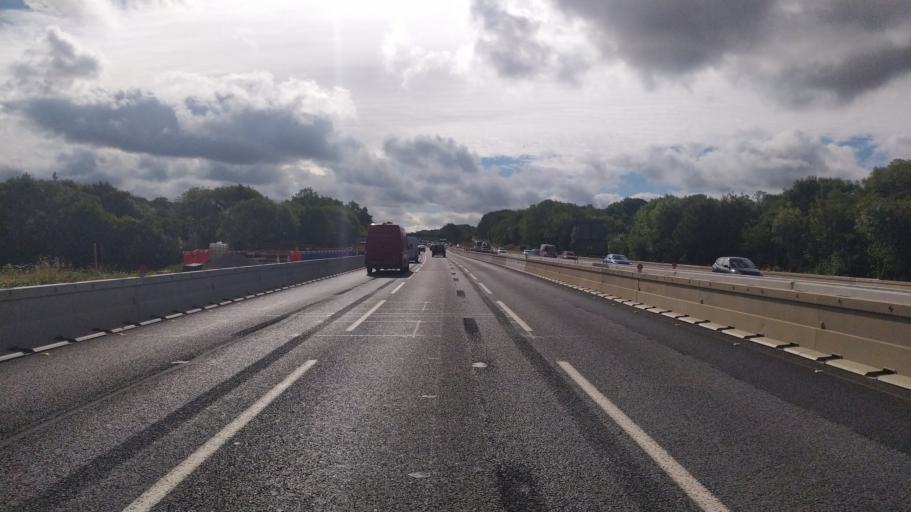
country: GB
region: England
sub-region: Hampshire
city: Fareham
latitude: 50.8626
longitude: -1.1670
